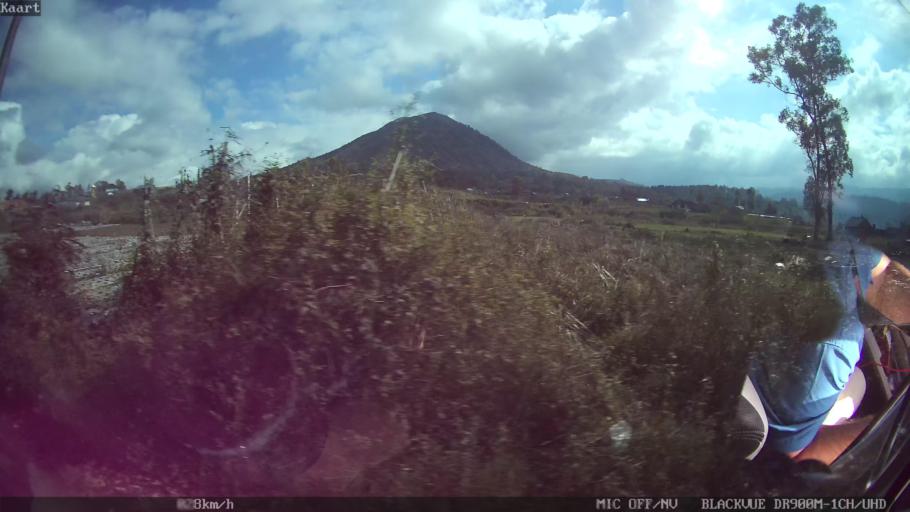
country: ID
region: Bali
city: Banjar Trunyan
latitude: -8.2199
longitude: 115.3939
